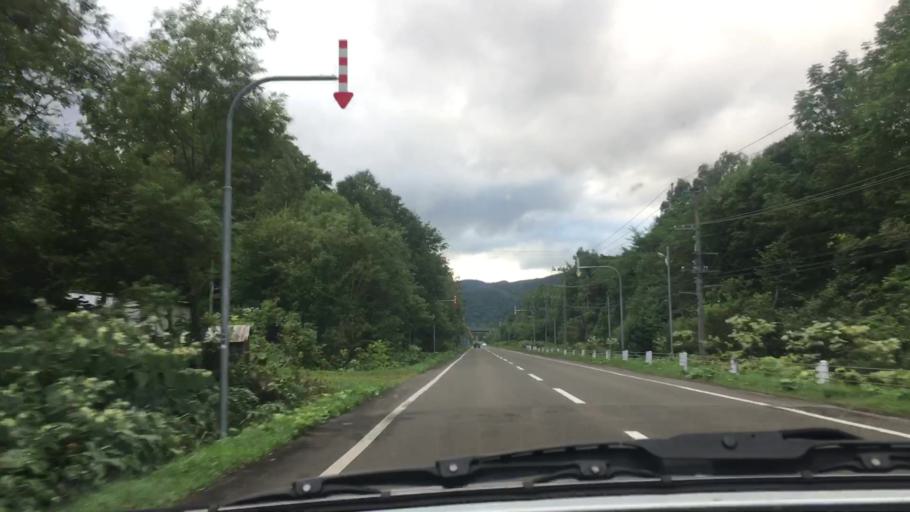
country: JP
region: Hokkaido
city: Shimo-furano
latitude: 43.0561
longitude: 142.5732
